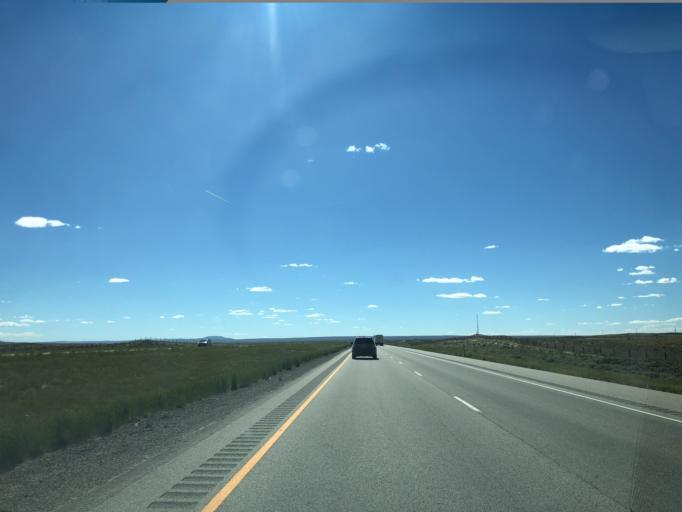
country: US
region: Wyoming
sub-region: Sweetwater County
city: Rock Springs
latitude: 41.6313
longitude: -108.3337
